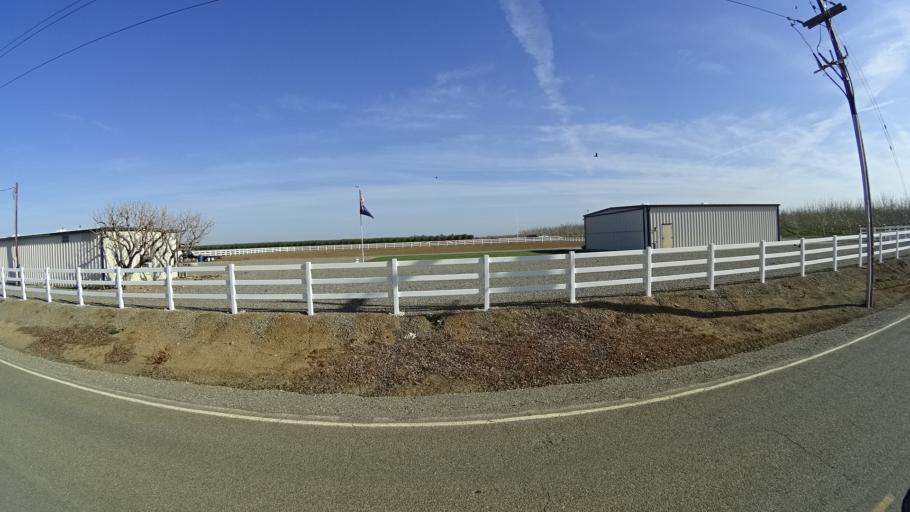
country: US
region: California
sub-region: Glenn County
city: Willows
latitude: 39.5388
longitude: -122.2316
